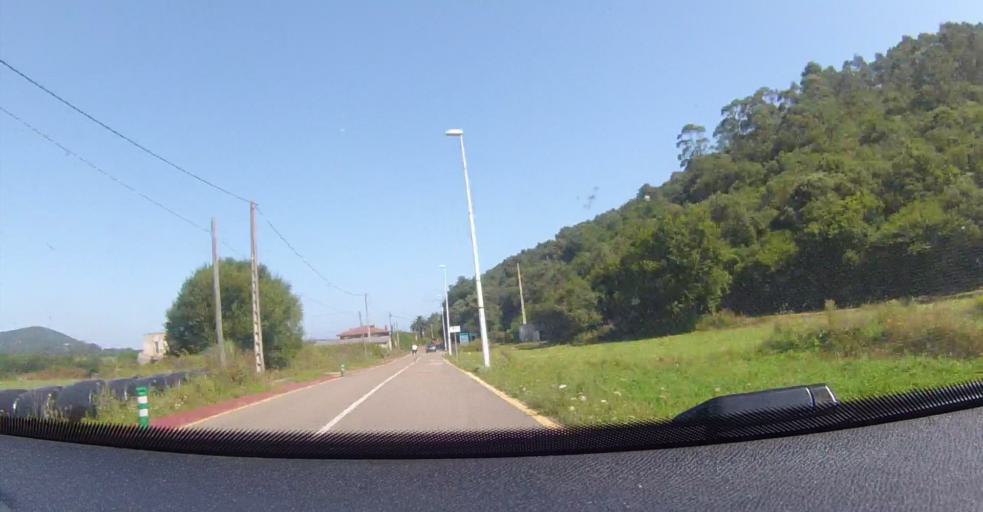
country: ES
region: Cantabria
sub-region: Provincia de Cantabria
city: Noja
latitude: 43.4628
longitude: -3.5192
